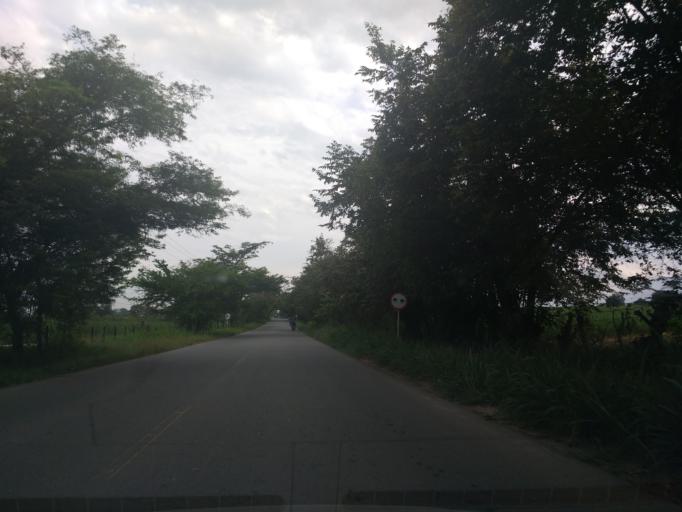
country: CO
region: Valle del Cauca
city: Florida
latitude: 3.2954
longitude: -76.2292
